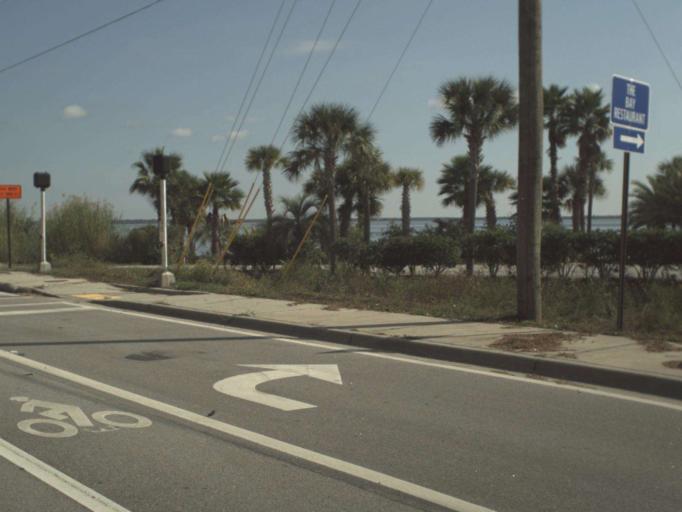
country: US
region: Florida
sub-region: Walton County
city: Seaside
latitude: 30.3874
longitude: -86.1745
